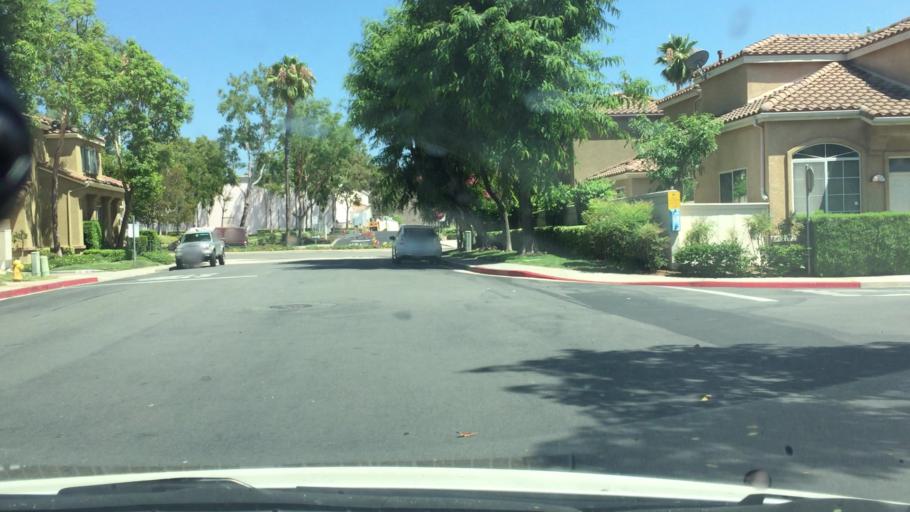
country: US
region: California
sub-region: Orange County
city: Rancho Santa Margarita
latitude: 33.6373
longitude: -117.5937
